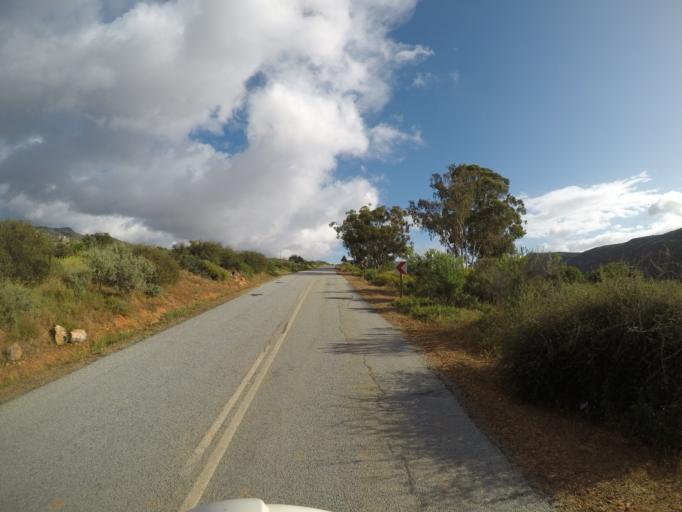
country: ZA
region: Western Cape
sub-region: West Coast District Municipality
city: Clanwilliam
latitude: -32.4326
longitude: 18.9395
